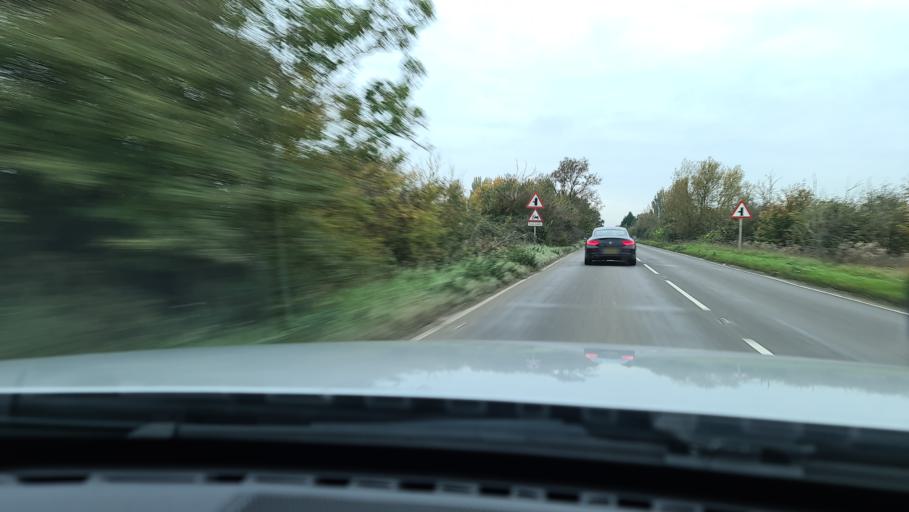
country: GB
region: England
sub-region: Buckinghamshire
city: Steeple Claydon
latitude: 51.8726
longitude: -1.0478
